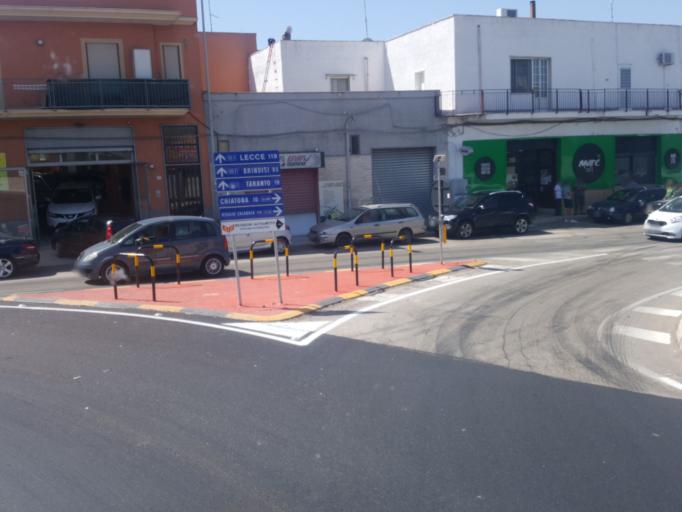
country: IT
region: Apulia
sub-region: Provincia di Taranto
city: Massafra
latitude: 40.5858
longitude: 17.1078
